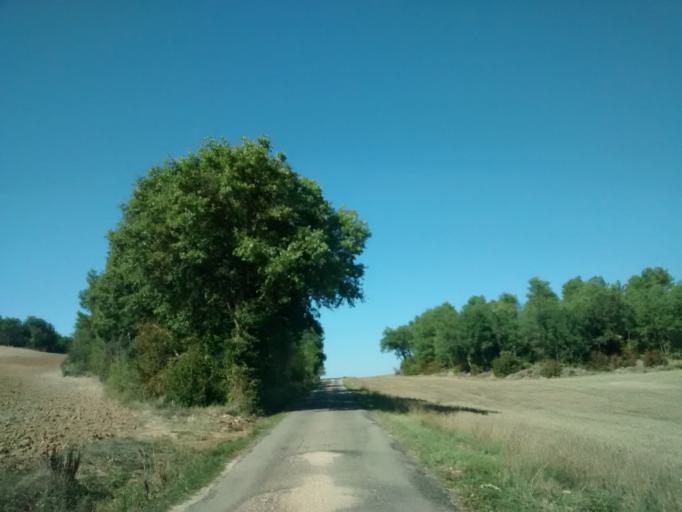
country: ES
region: Aragon
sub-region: Provincia de Huesca
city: Santa Cruz de la Seros
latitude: 42.4331
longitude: -0.6345
